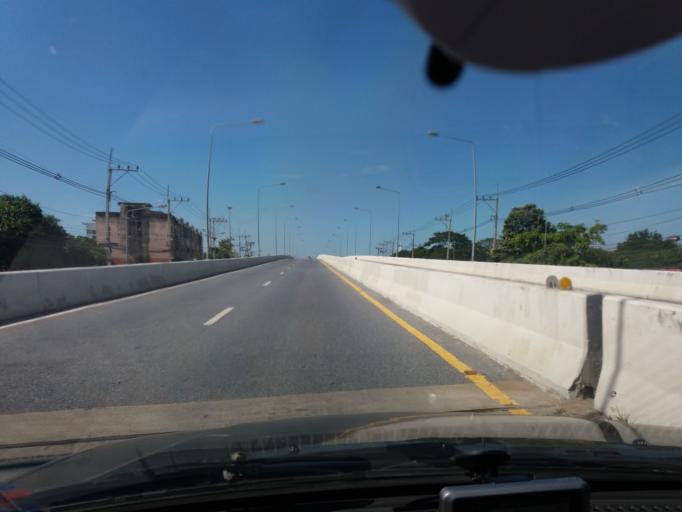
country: TH
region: Suphan Buri
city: Suphan Buri
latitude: 14.4647
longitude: 100.1336
